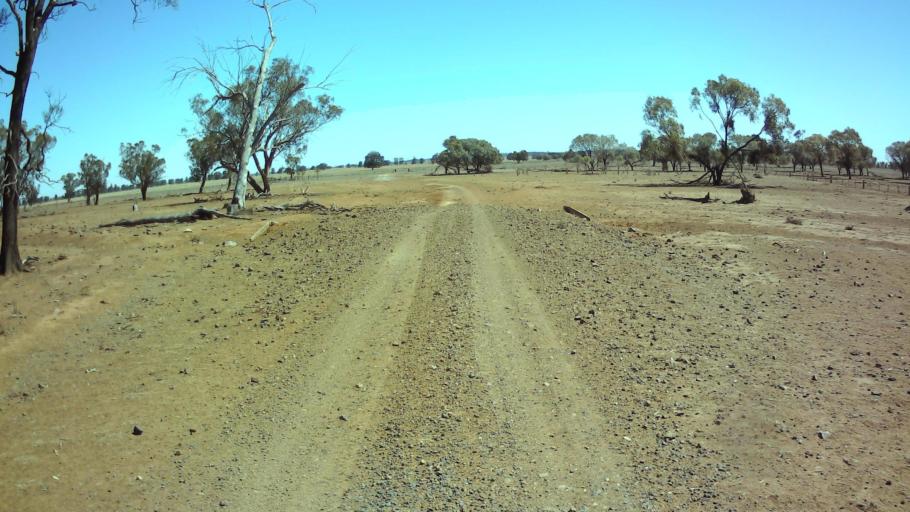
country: AU
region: New South Wales
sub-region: Forbes
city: Forbes
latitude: -33.7268
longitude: 147.6656
